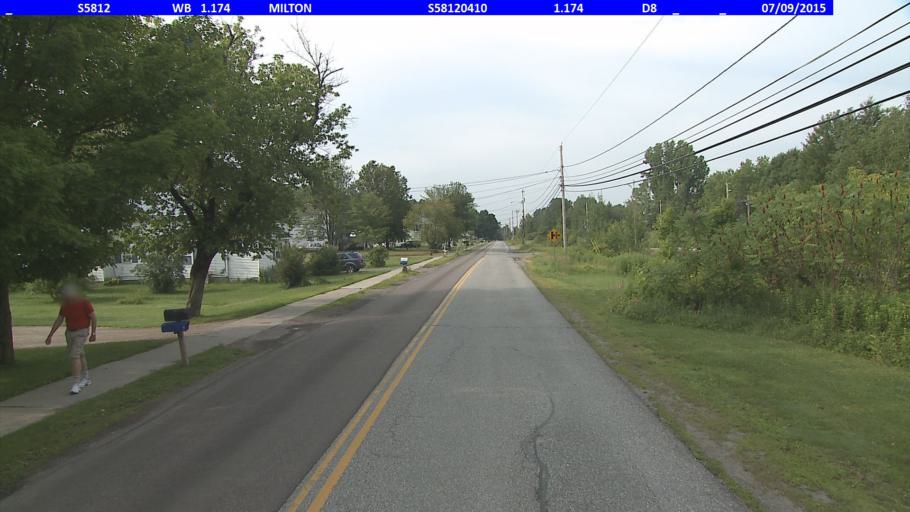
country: US
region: Vermont
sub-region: Chittenden County
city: Milton
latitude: 44.6354
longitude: -73.1056
